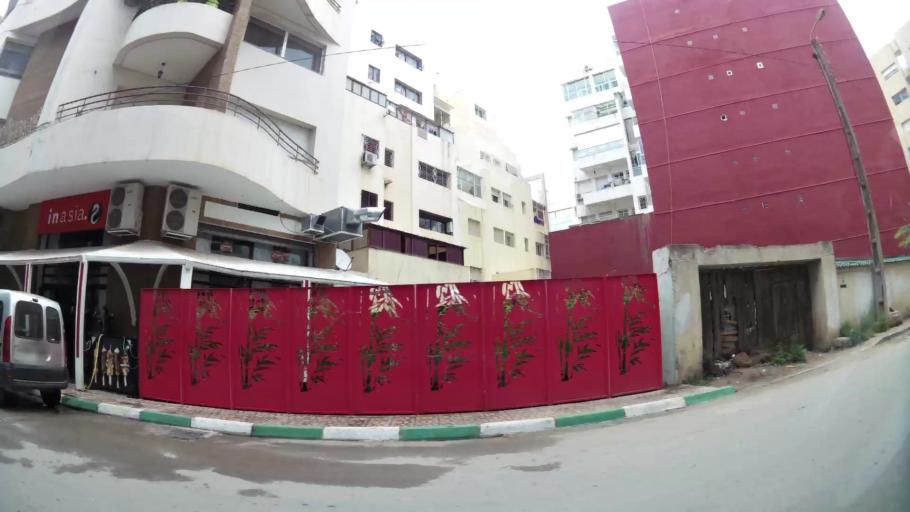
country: MA
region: Fes-Boulemane
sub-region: Fes
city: Fes
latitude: 34.0309
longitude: -5.0058
